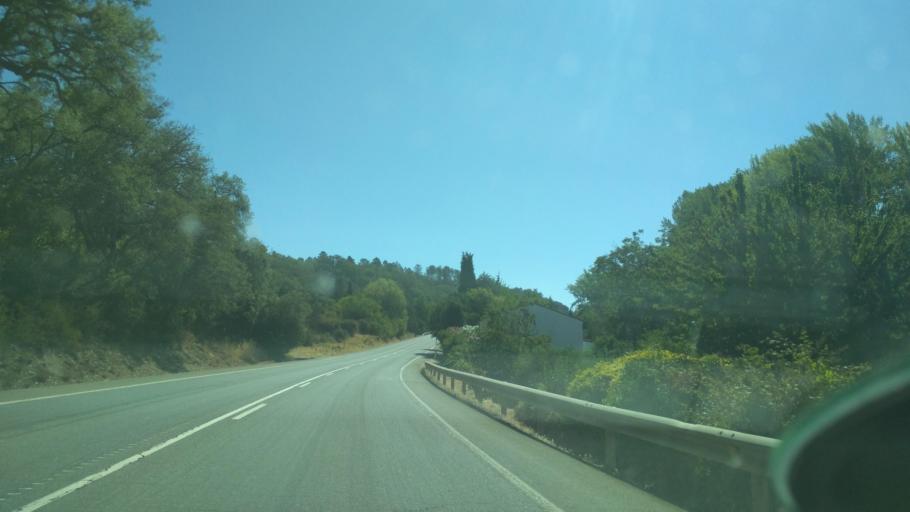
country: ES
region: Andalusia
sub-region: Provincia de Huelva
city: Fuenteheridos
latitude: 37.9165
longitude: -6.6764
